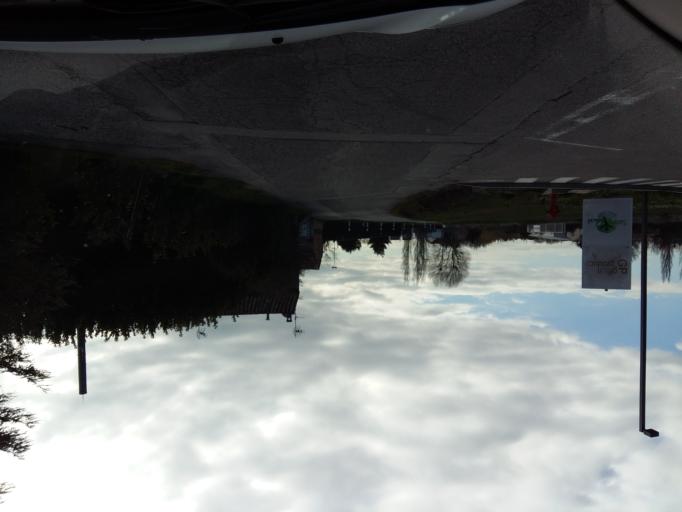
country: FR
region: Provence-Alpes-Cote d'Azur
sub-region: Departement du Vaucluse
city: Cheval-Blanc
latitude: 43.8112
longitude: 5.0484
